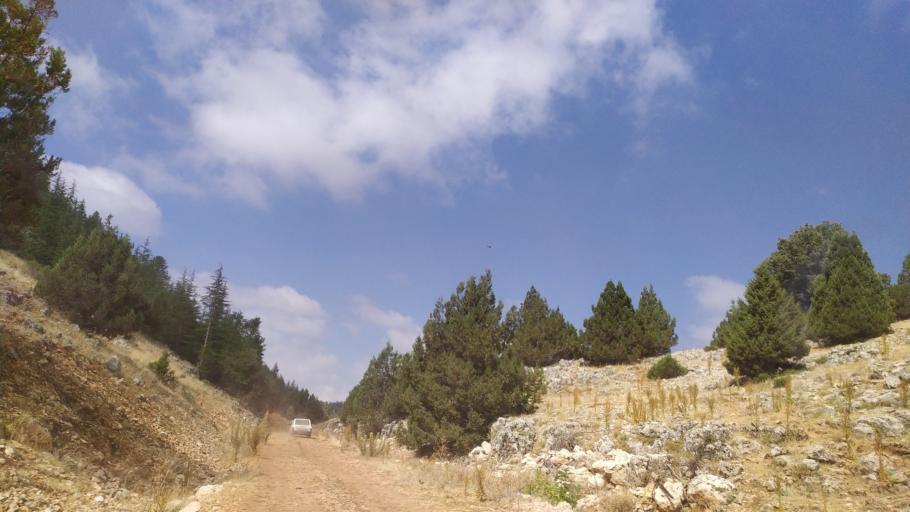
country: TR
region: Mersin
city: Kirobasi
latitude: 36.6167
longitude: 33.8312
